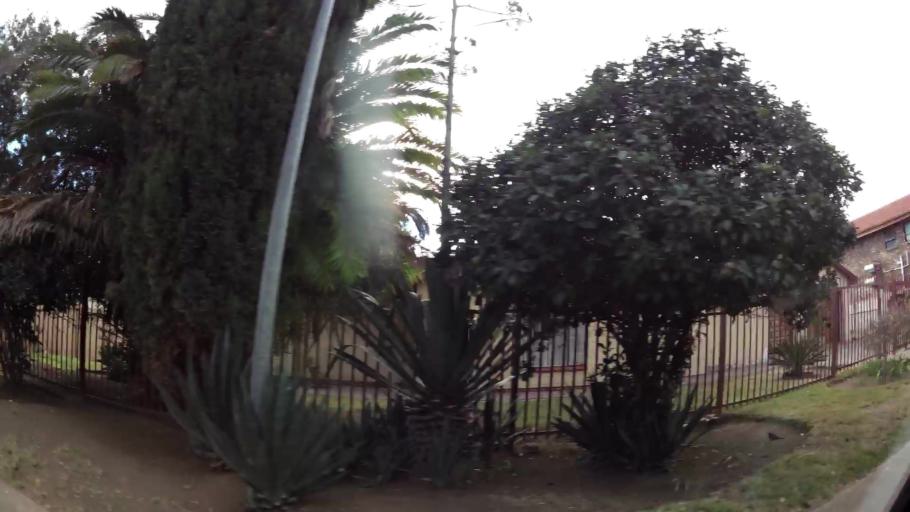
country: ZA
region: Limpopo
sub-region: Capricorn District Municipality
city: Polokwane
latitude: -23.9170
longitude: 29.4466
